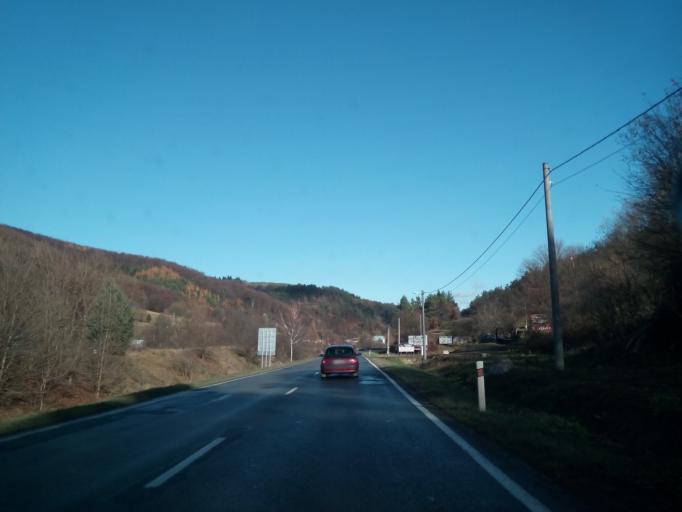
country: SK
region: Presovsky
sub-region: Okres Bardejov
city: Bardejov
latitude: 49.2617
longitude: 21.2514
